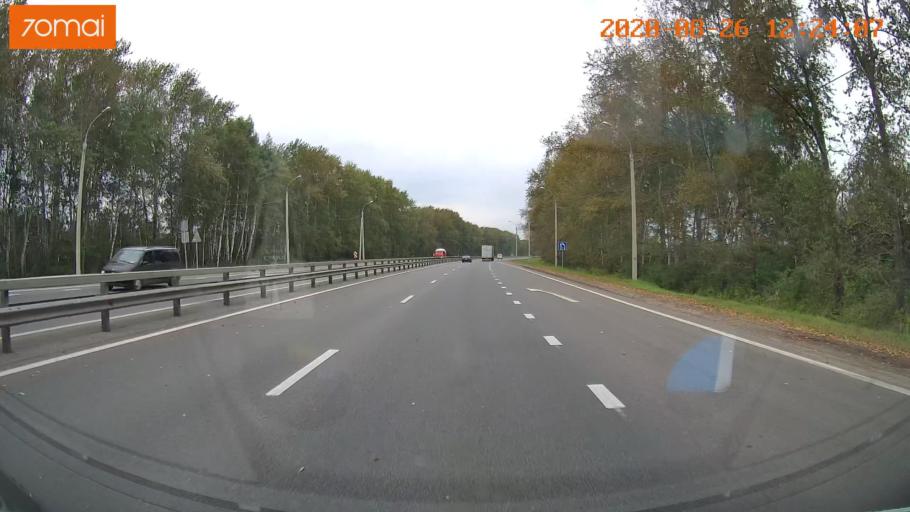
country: RU
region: Rjazan
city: Murmino
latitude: 54.5107
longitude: 39.8982
